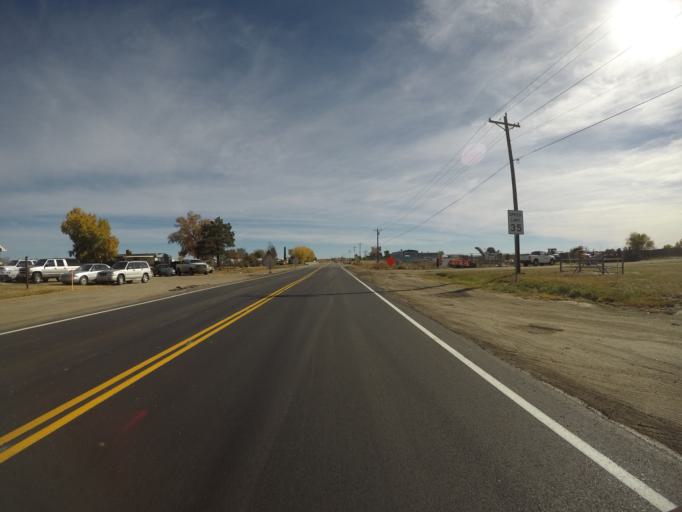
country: US
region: Colorado
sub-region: Adams County
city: Strasburg
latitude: 39.7384
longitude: -104.3209
